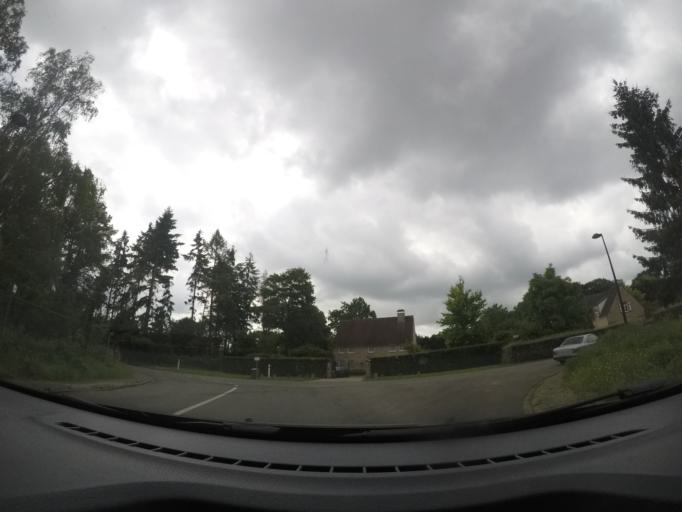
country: BE
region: Flanders
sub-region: Provincie Vlaams-Brabant
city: Sint-Genesius-Rode
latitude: 50.7499
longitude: 4.3493
